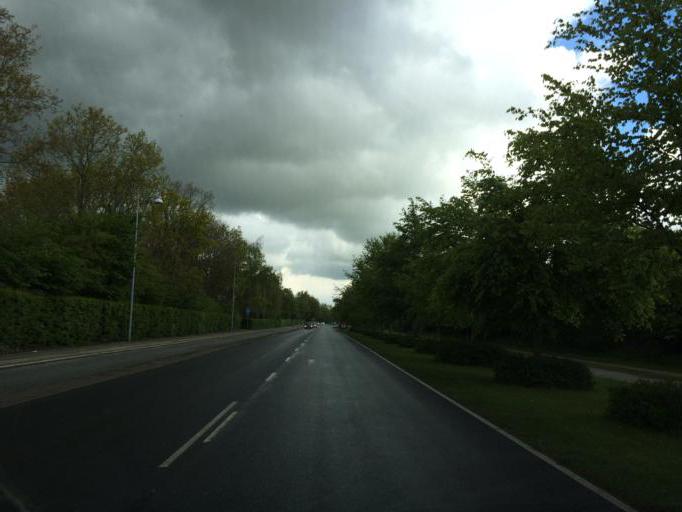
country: DK
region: Central Jutland
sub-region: Holstebro Kommune
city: Holstebro
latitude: 56.3708
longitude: 8.6110
